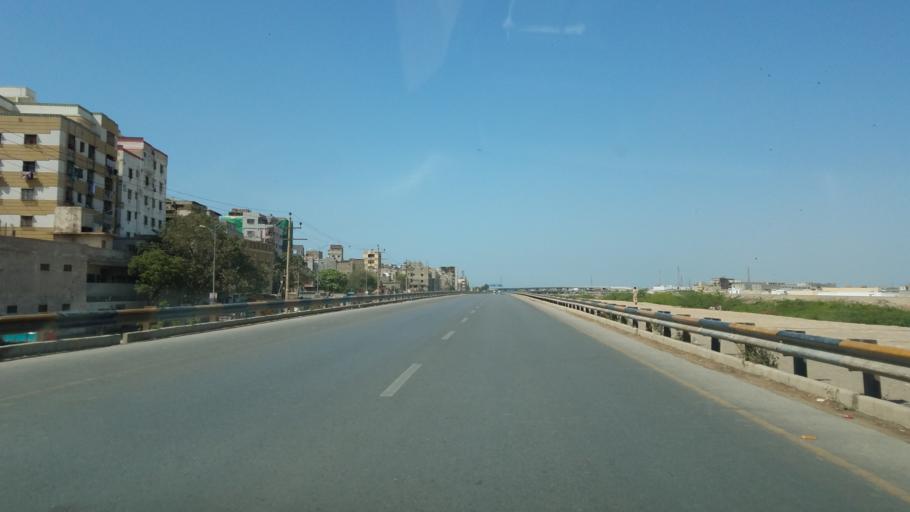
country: PK
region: Sindh
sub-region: Karachi District
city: Karachi
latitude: 24.8757
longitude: 66.9860
